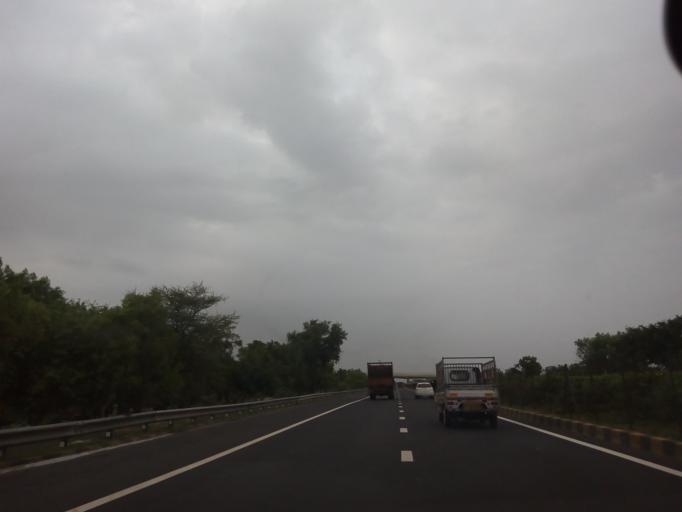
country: IN
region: Gujarat
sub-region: Kheda
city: Mahemdavad
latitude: 22.8618
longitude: 72.8075
